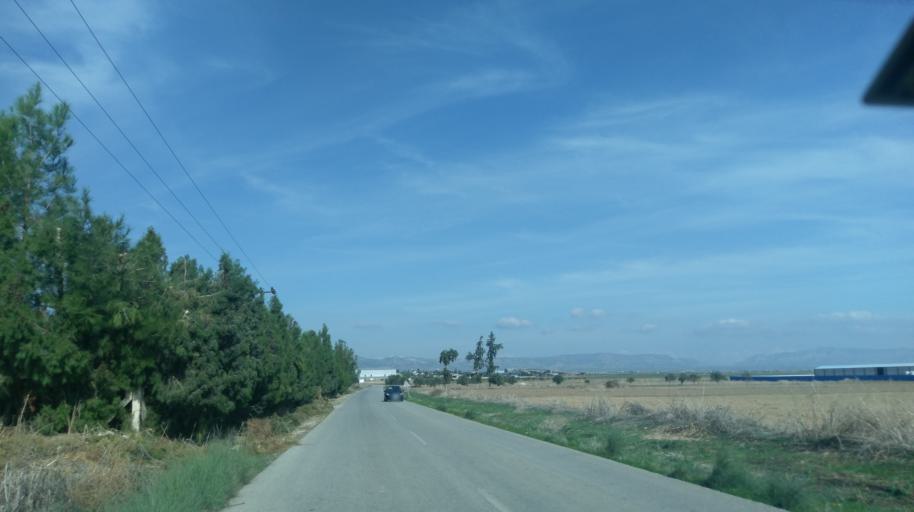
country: CY
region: Ammochostos
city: Lefkonoiko
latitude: 35.2084
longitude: 33.6194
